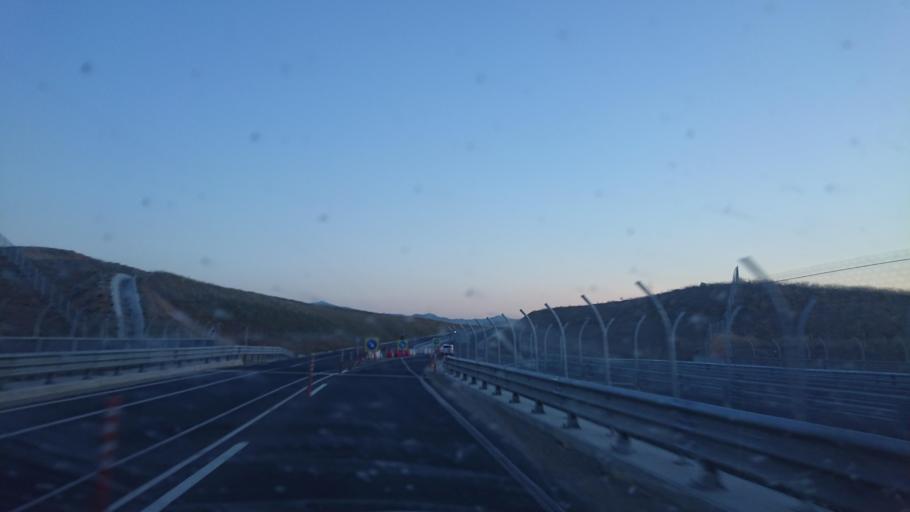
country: TR
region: Aksaray
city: Balci
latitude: 38.7824
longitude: 34.1174
